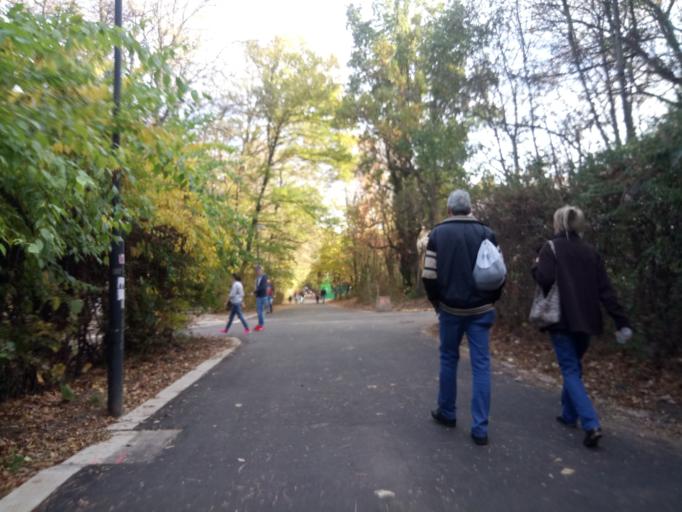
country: BG
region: Sofia-Capital
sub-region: Stolichna Obshtina
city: Sofia
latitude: 42.6780
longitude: 23.3459
